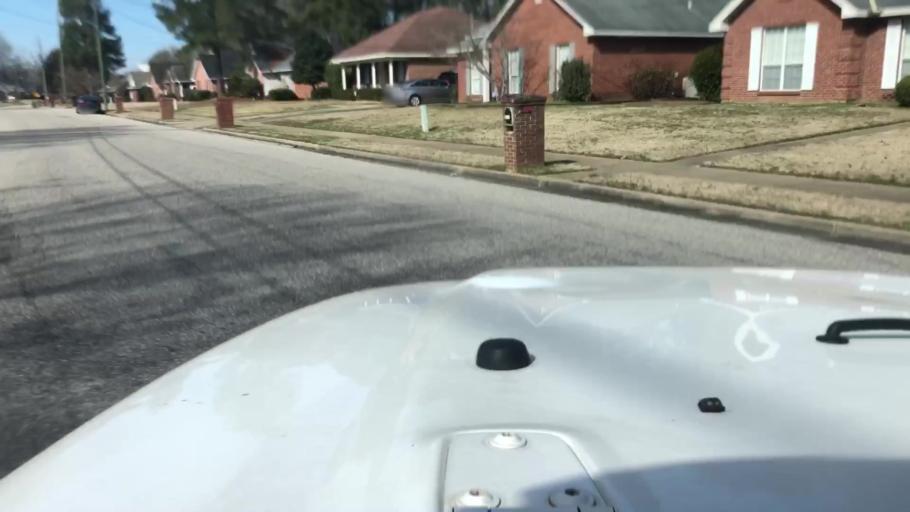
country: US
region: Alabama
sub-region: Elmore County
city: Blue Ridge
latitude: 32.4071
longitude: -86.1913
